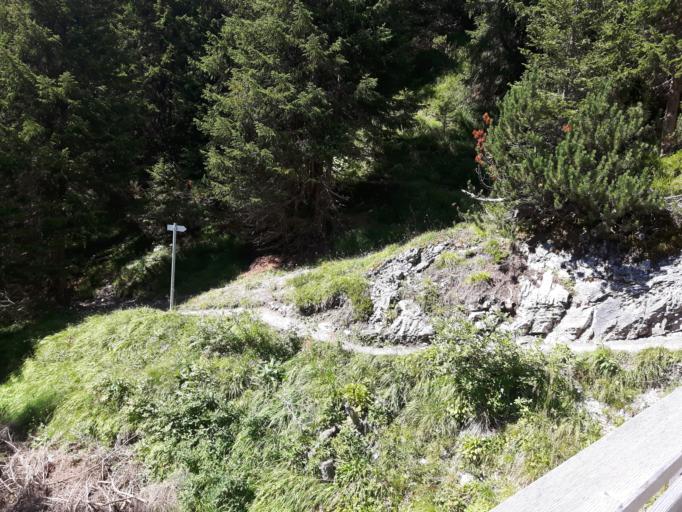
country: CH
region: Grisons
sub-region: Imboden District
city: Flims
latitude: 46.8600
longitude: 9.2520
